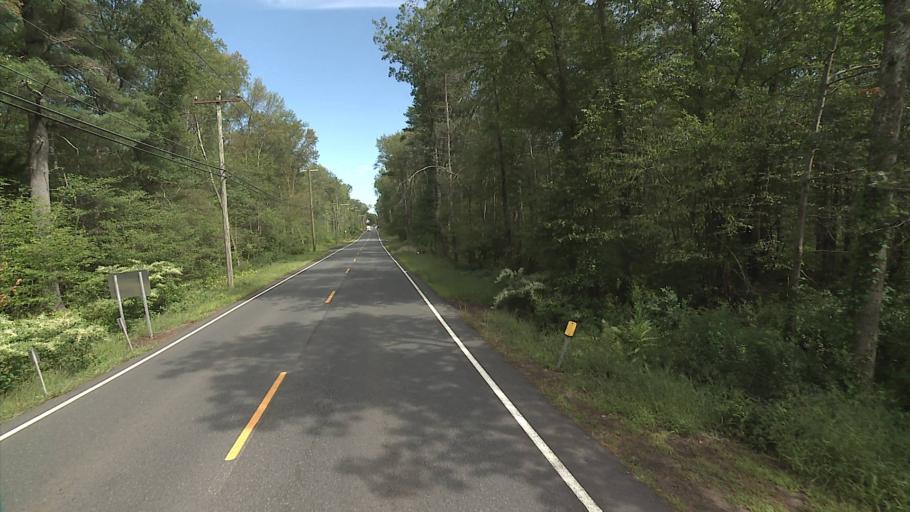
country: US
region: Connecticut
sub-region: Tolland County
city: Stafford Springs
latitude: 41.9680
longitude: -72.3152
